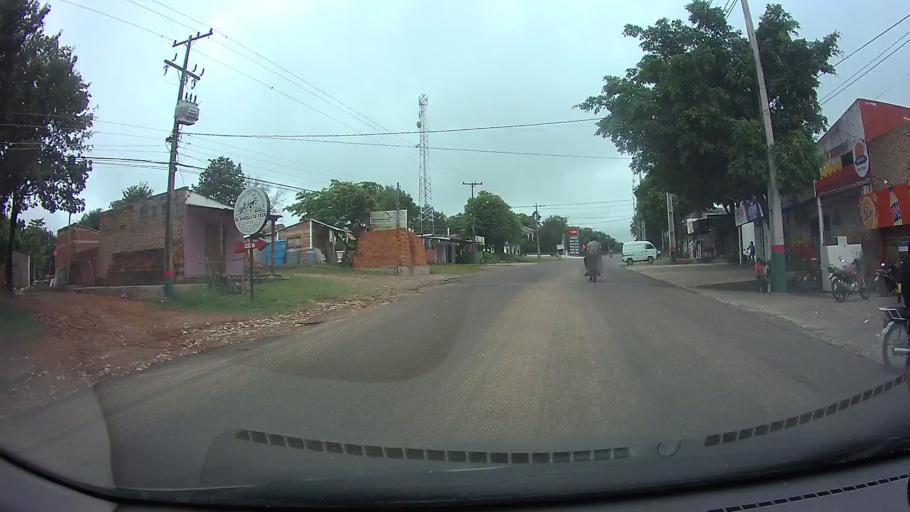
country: PY
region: Cordillera
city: Altos
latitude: -25.2684
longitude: -57.2529
